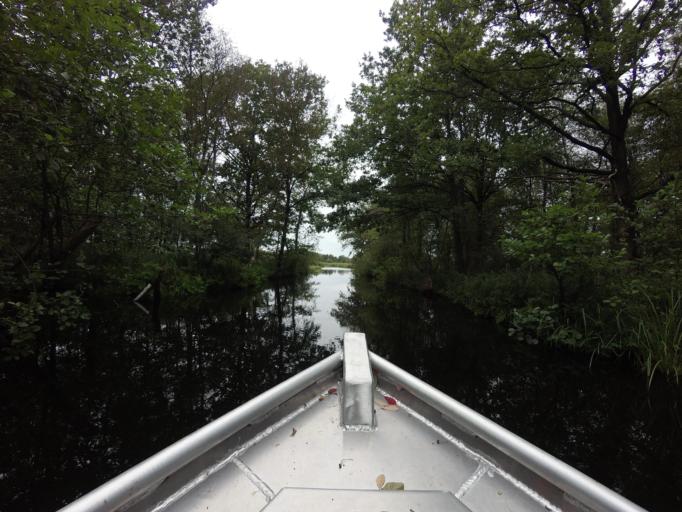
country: NL
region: Overijssel
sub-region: Gemeente Steenwijkerland
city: Oldemarkt
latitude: 52.7957
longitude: 5.9424
